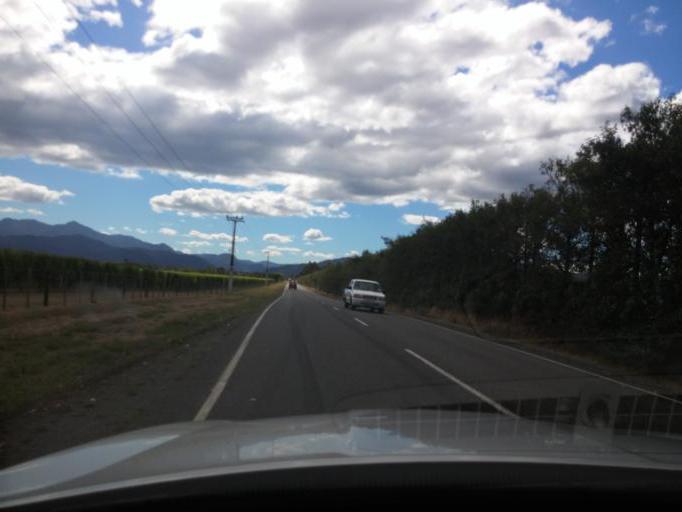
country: NZ
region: Marlborough
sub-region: Marlborough District
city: Blenheim
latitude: -41.5261
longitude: 173.8469
